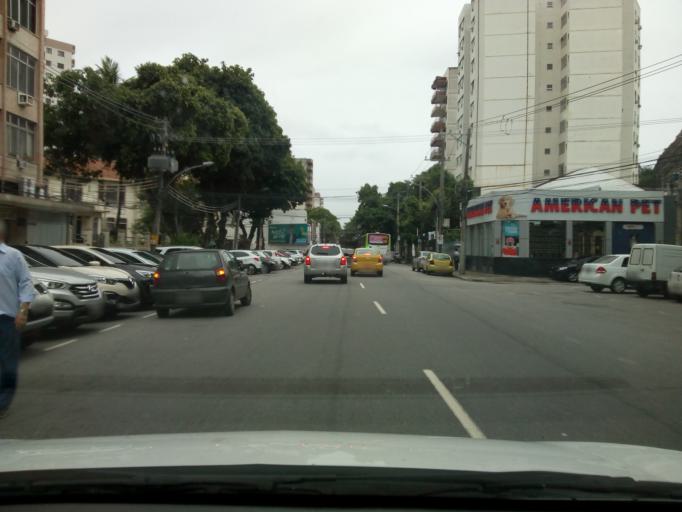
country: BR
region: Rio de Janeiro
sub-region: Rio De Janeiro
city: Rio de Janeiro
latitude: -22.9213
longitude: -43.2320
